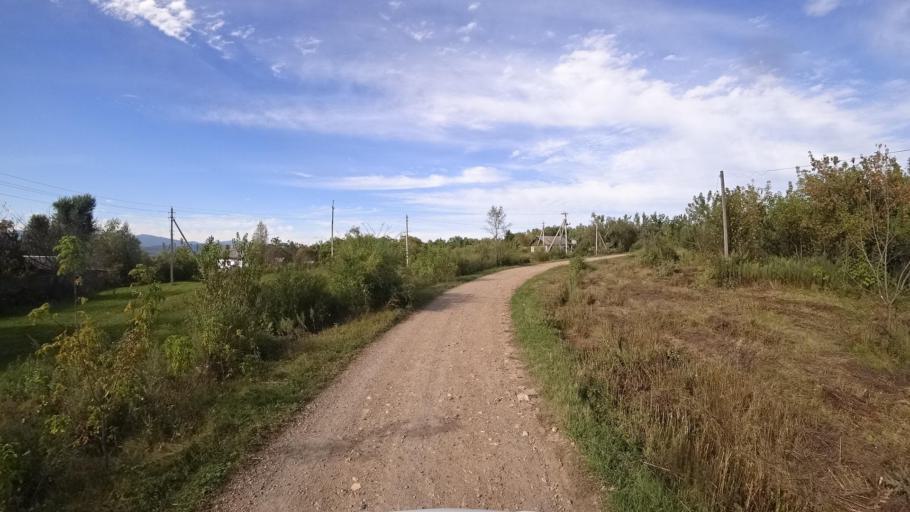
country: RU
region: Primorskiy
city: Dostoyevka
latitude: 44.2956
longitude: 133.4482
